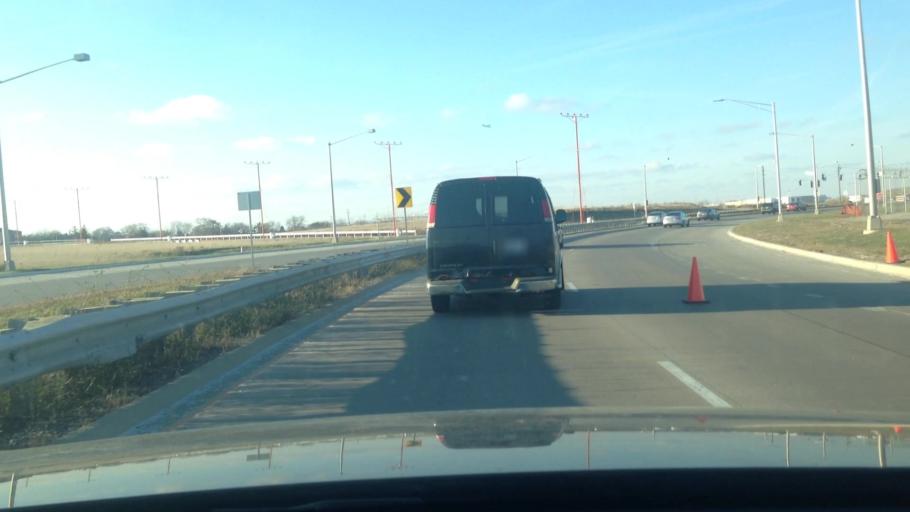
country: US
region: Illinois
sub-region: DuPage County
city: Bensenville
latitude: 41.9565
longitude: -87.9332
